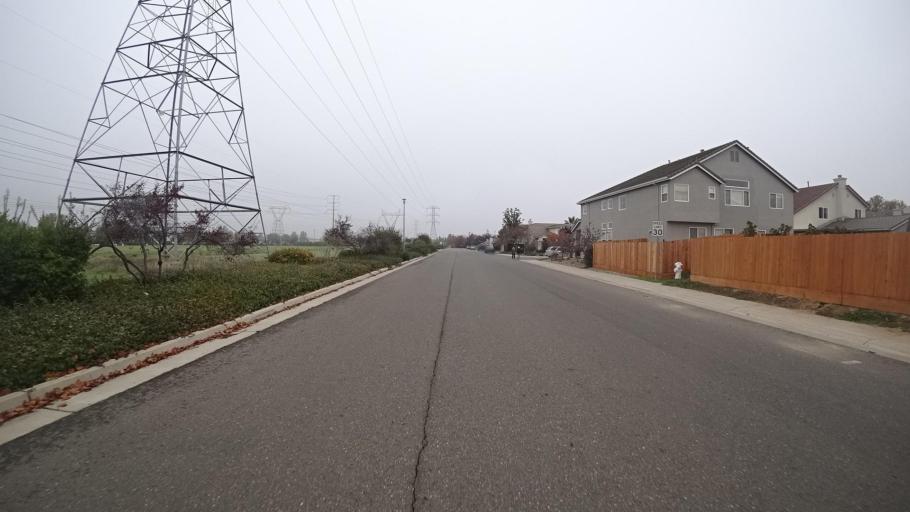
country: US
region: California
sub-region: Sacramento County
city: Elk Grove
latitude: 38.4047
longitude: -121.3493
